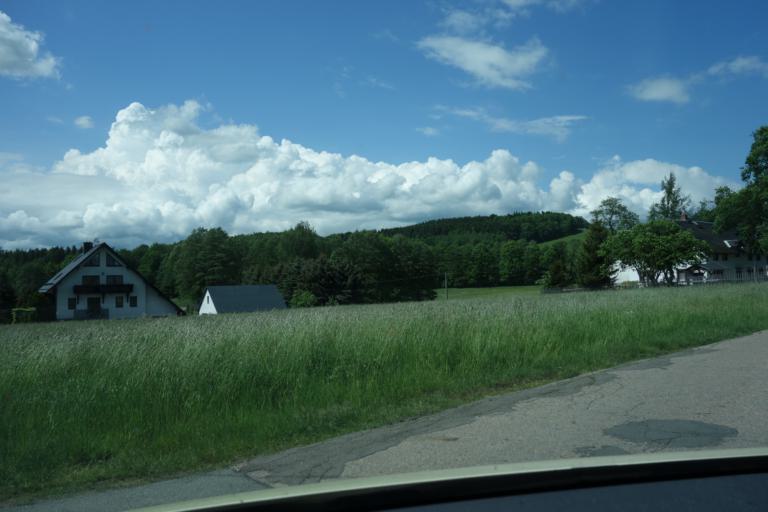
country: DE
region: Saxony
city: Eppendorf
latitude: 50.7987
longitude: 13.2794
